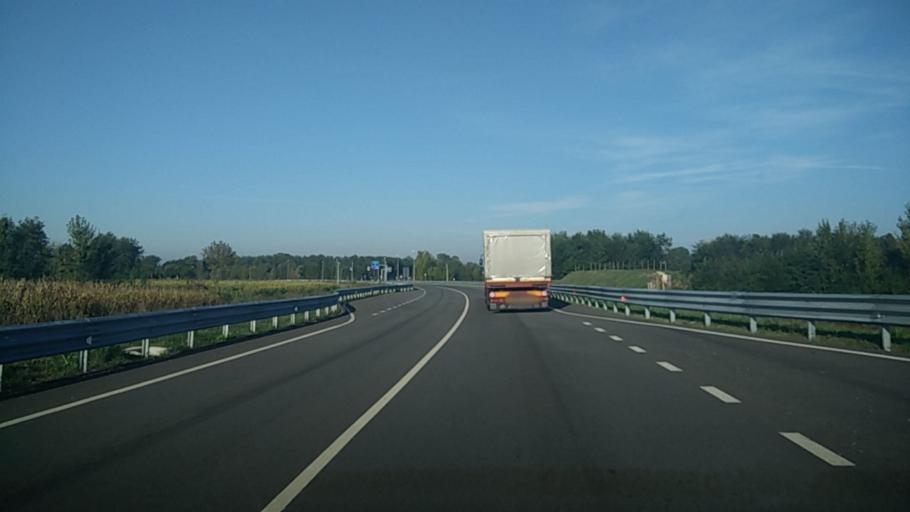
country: IT
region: Veneto
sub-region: Provincia di Venezia
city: Peseggia-Gardigiano
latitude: 45.5509
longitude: 12.1765
